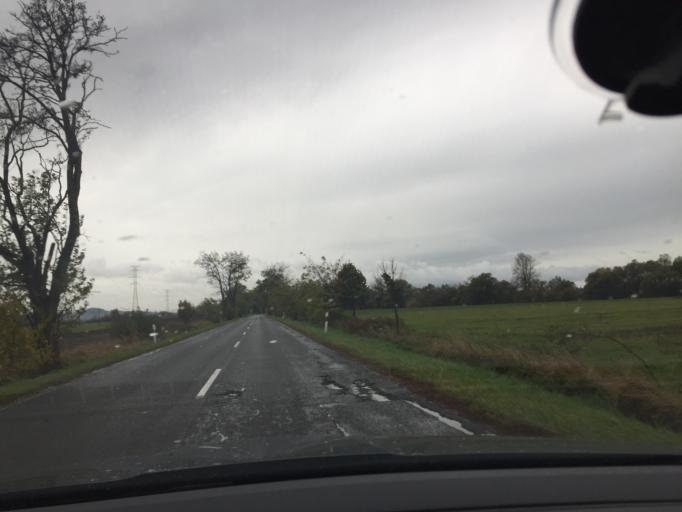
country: SK
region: Nitriansky
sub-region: Okres Nove Zamky
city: Sturovo
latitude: 47.7749
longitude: 18.7235
